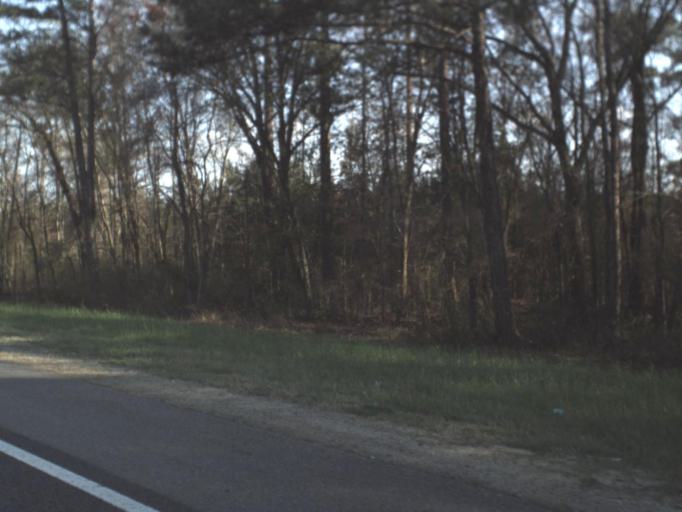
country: US
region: Florida
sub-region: Gadsden County
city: Midway
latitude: 30.4871
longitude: -84.4174
